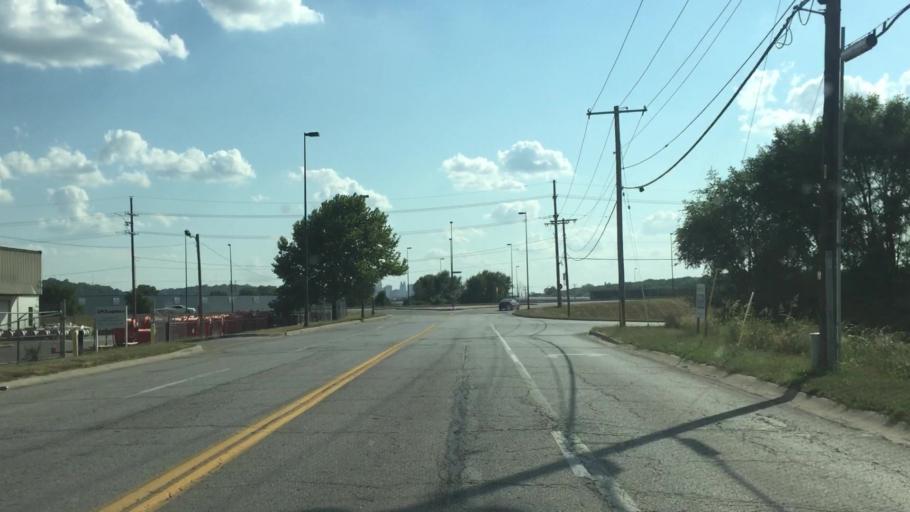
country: US
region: Missouri
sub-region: Clay County
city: North Kansas City
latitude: 39.1384
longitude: -94.5275
